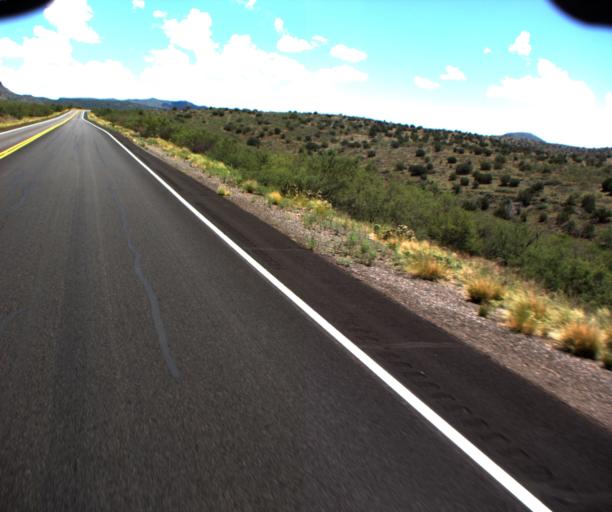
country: US
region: Arizona
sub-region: Yavapai County
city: Camp Verde
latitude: 34.5078
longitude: -111.7352
